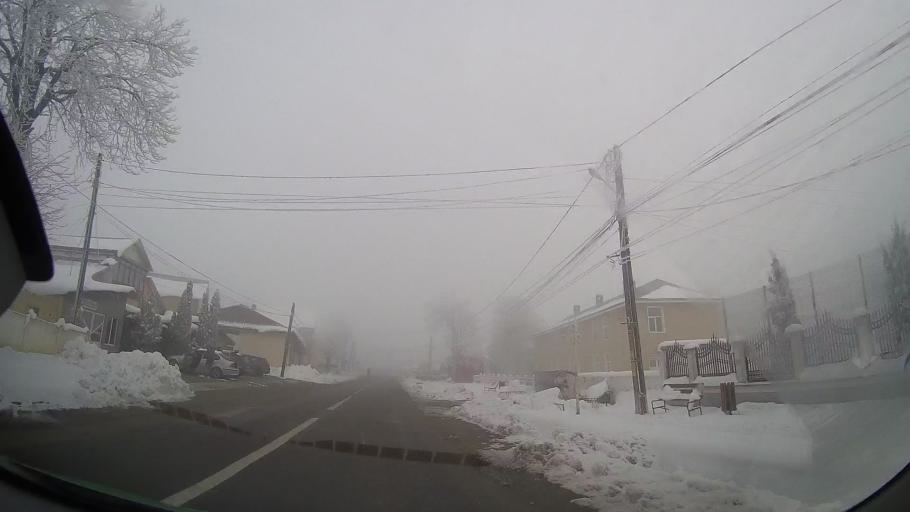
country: RO
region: Neamt
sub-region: Comuna Sabaoani
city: Sabaoani
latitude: 47.0152
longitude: 26.8649
